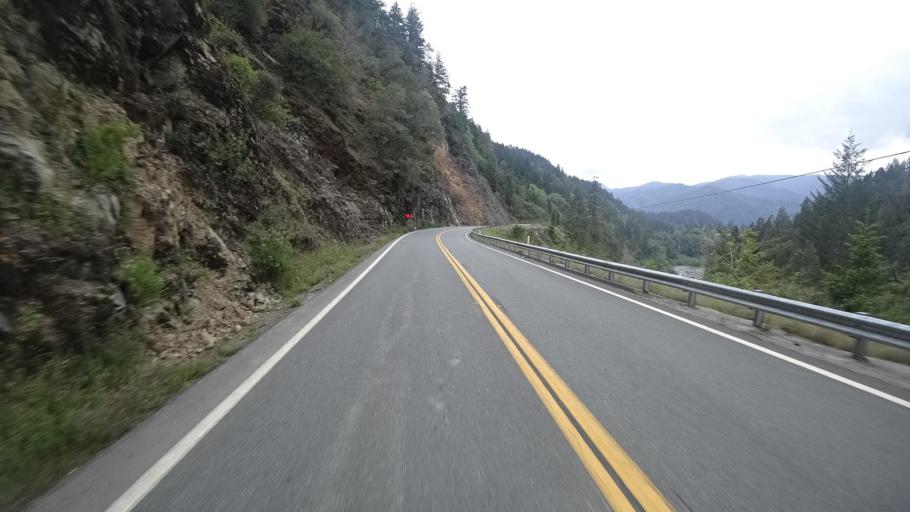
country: US
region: California
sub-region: Humboldt County
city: Willow Creek
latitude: 41.1106
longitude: -123.6862
